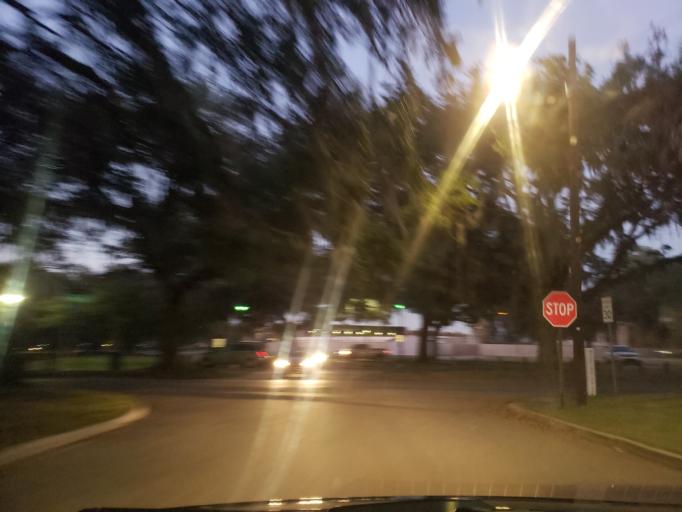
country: US
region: Georgia
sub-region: Chatham County
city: Thunderbolt
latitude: 32.0428
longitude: -81.0796
